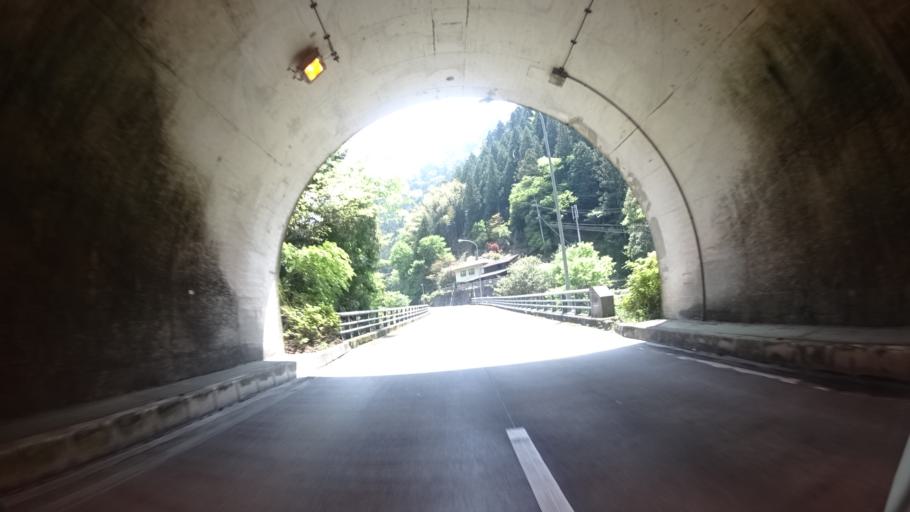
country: JP
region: Tokushima
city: Wakimachi
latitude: 33.9742
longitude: 134.0804
